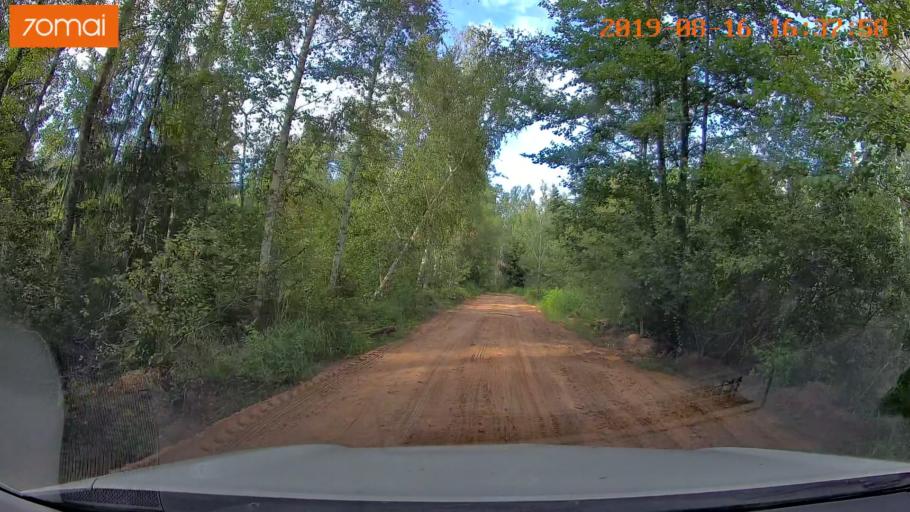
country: BY
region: Mogilev
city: Asipovichy
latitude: 53.2330
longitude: 28.7770
